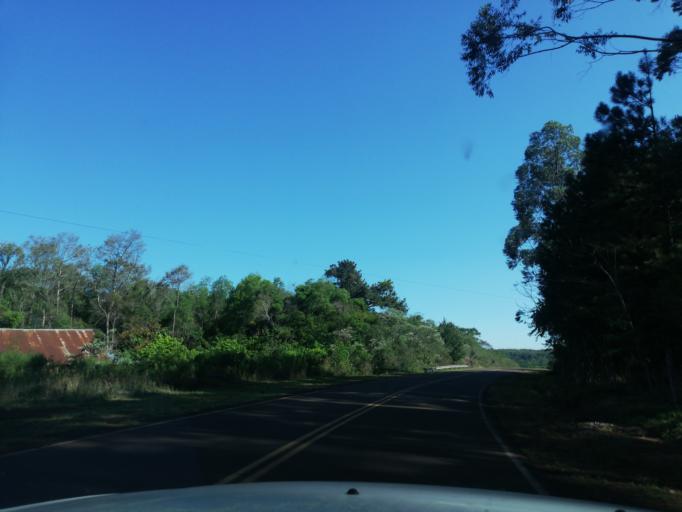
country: AR
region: Misiones
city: Arroyo del Medio
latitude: -27.6512
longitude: -55.4008
